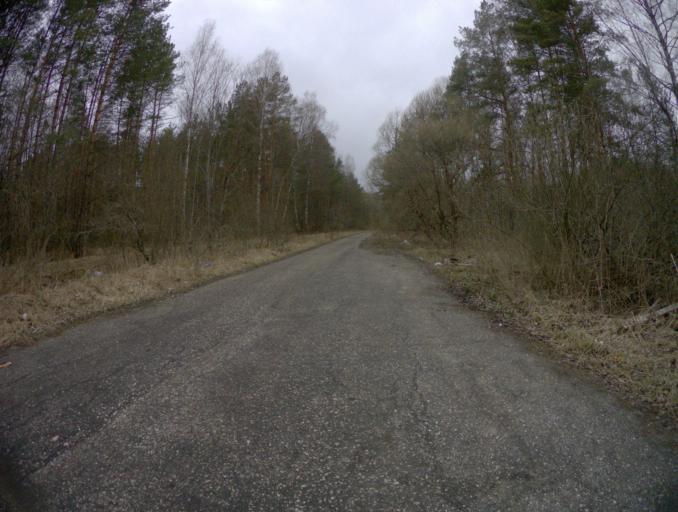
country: RU
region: Vladimir
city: Sudogda
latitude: 55.9739
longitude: 40.8161
